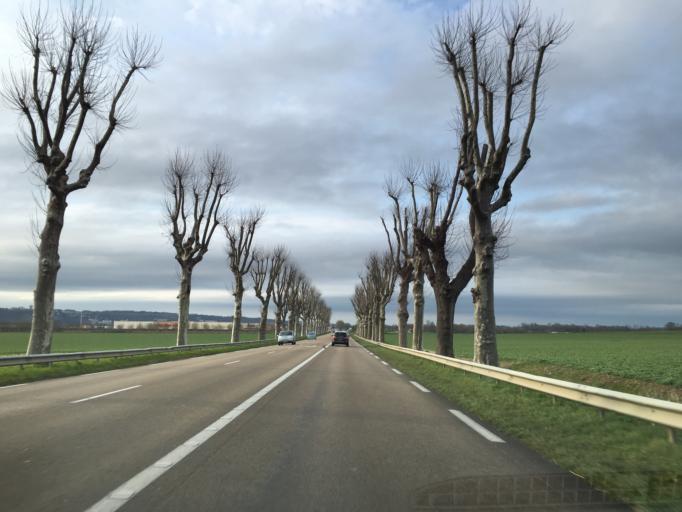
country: FR
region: Bourgogne
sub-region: Departement de l'Yonne
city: Maillot
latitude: 48.1659
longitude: 3.2993
